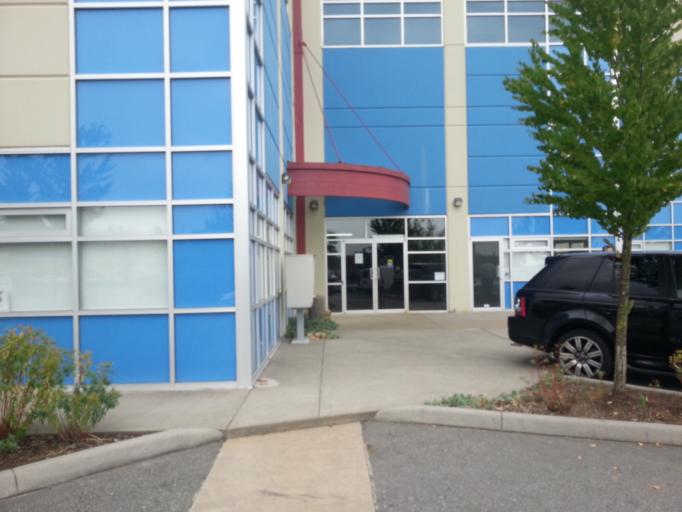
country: CA
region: British Columbia
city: Langley
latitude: 49.0990
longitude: -122.7088
